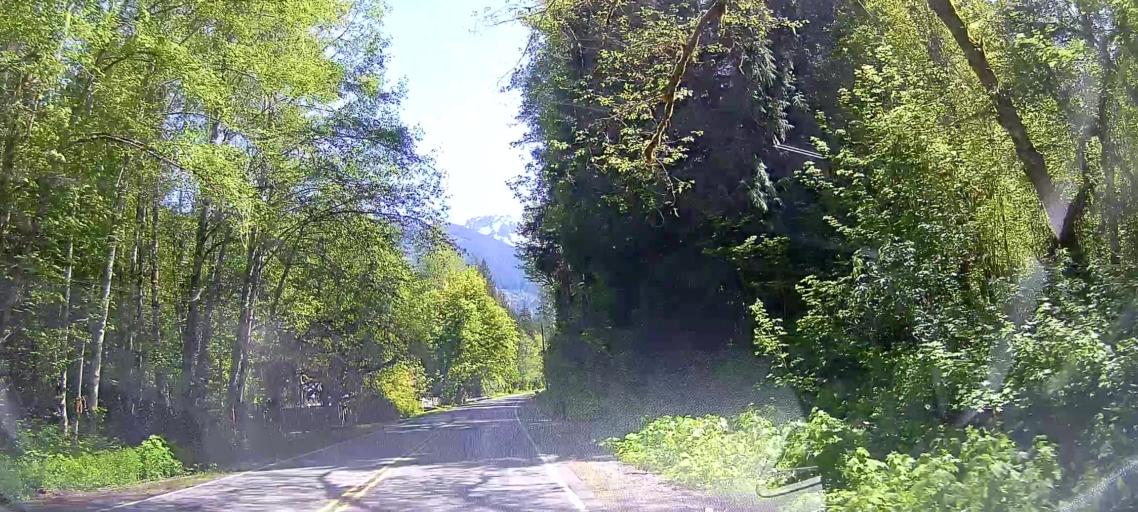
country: US
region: Washington
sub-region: Snohomish County
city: Darrington
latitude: 48.5095
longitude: -121.6828
